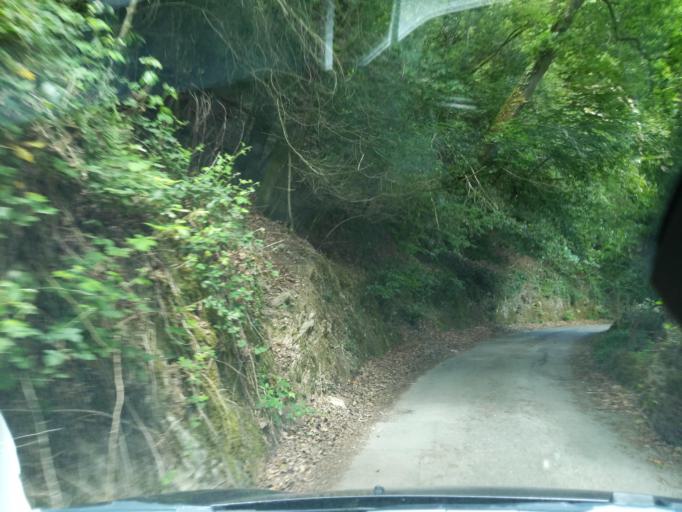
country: GB
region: England
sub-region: Devon
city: Plympton
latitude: 50.4083
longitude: -4.0857
